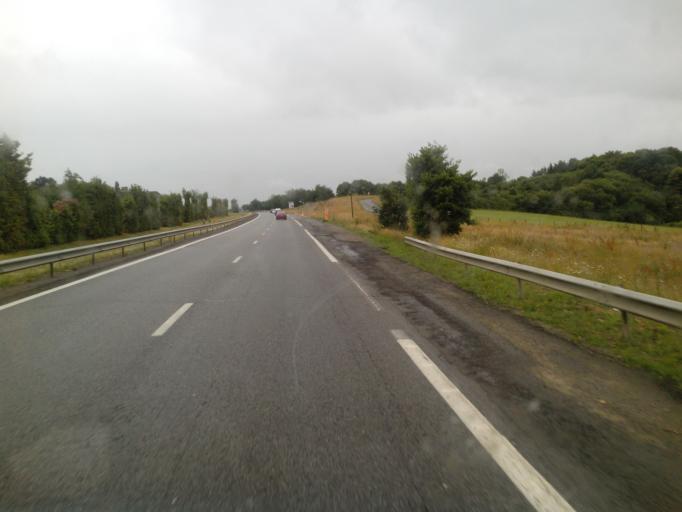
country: FR
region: Brittany
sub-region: Departement d'Ille-et-Vilaine
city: Crevin
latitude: 47.9168
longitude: -1.6810
